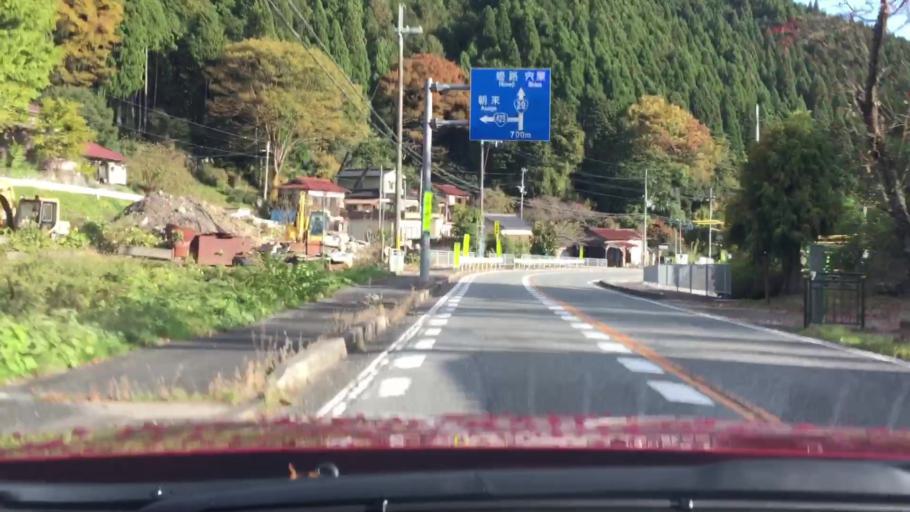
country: JP
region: Hyogo
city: Yamazakicho-nakabirose
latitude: 35.1729
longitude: 134.5435
